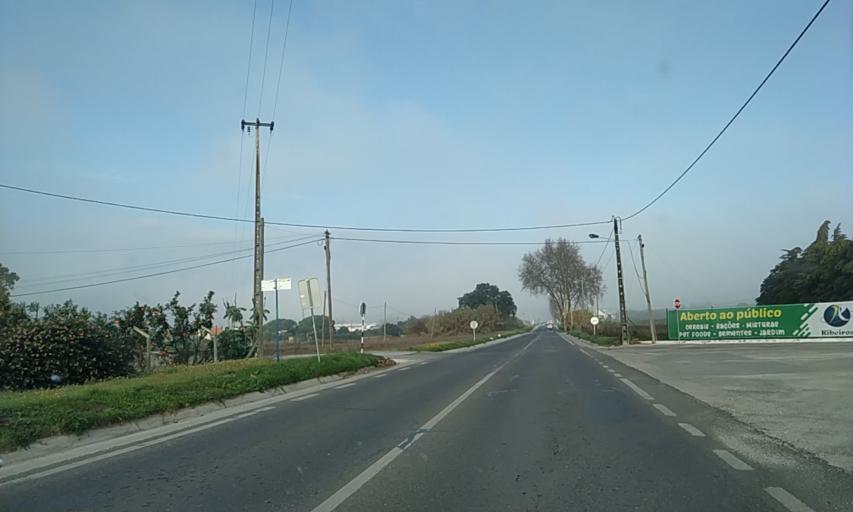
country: PT
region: Setubal
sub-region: Palmela
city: Pinhal Novo
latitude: 38.6694
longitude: -8.9299
